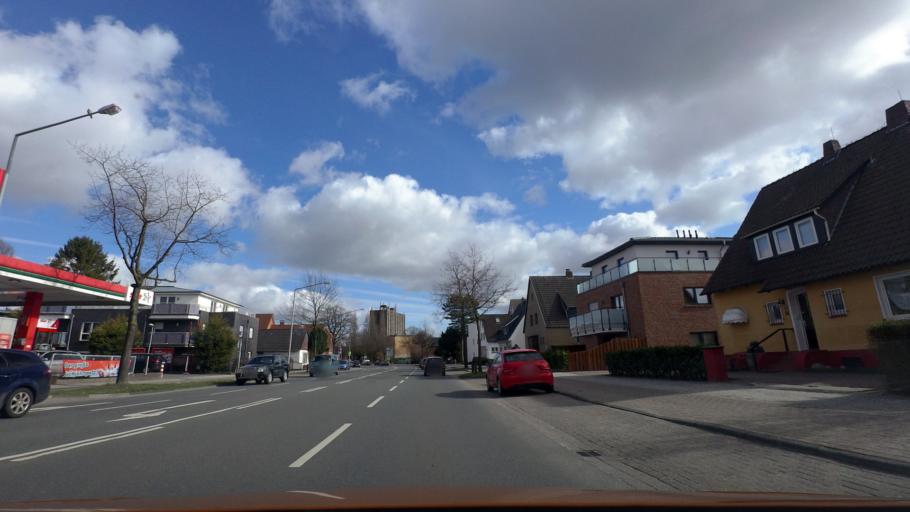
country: DE
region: Lower Saxony
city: Oldenburg
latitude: 53.1413
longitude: 8.1724
